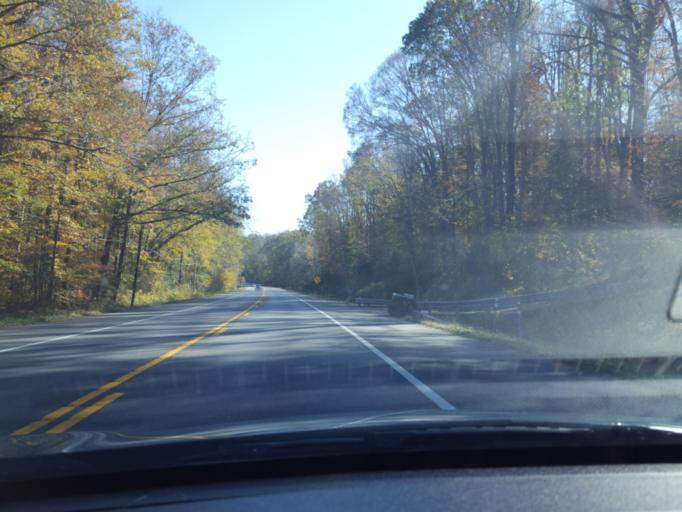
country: US
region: Maryland
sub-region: Saint Mary's County
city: Leonardtown
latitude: 38.2636
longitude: -76.6049
